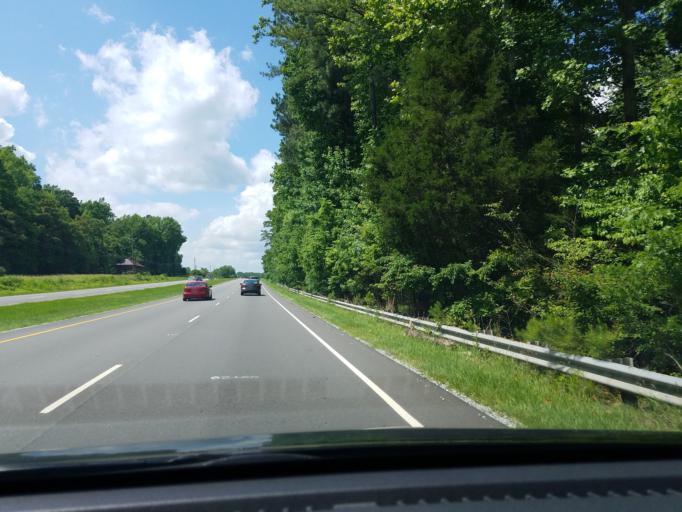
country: US
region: North Carolina
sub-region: Durham County
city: Gorman
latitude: 36.1302
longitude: -78.9029
